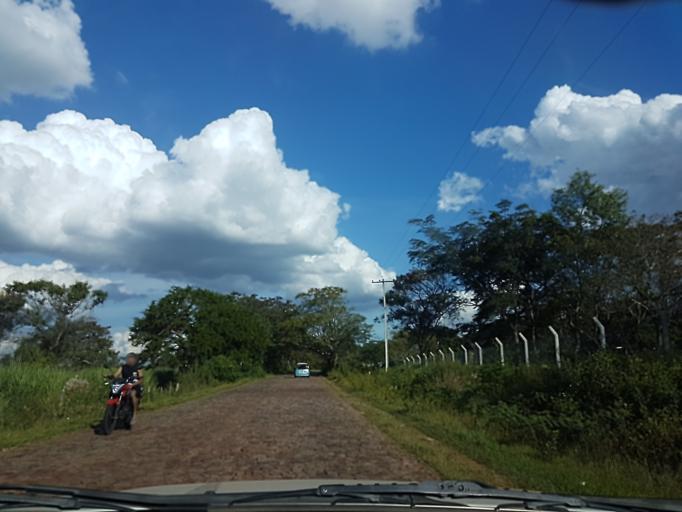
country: PY
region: Cordillera
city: Arroyos y Esteros
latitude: -24.9989
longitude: -57.1377
